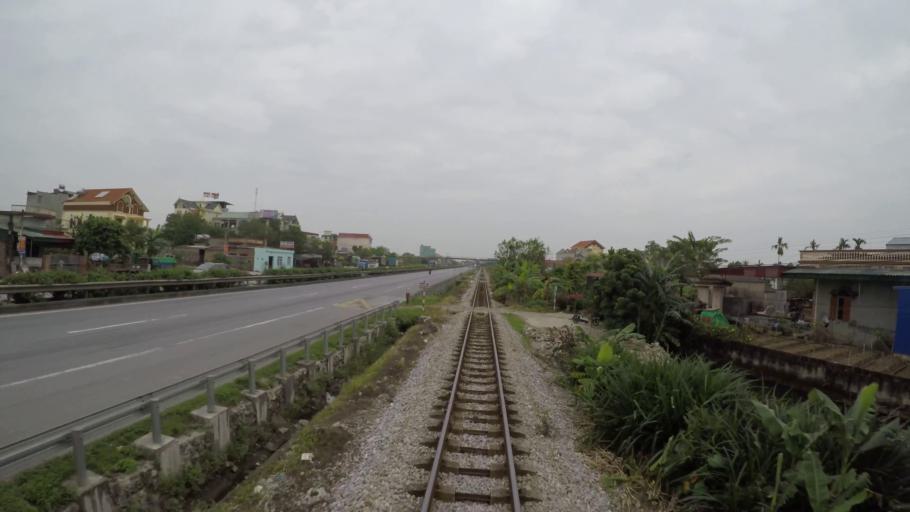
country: VN
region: Hai Duong
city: Phu Thai
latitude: 20.9570
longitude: 106.5259
